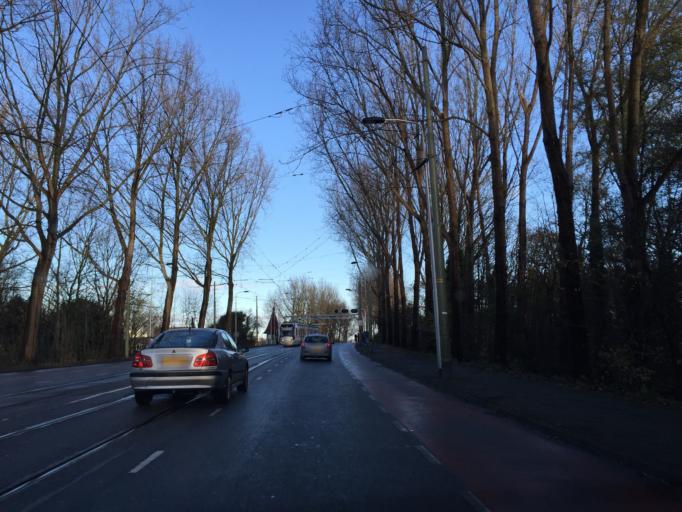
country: NL
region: South Holland
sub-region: Gemeente Delft
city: Delft
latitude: 52.0184
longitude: 4.3529
